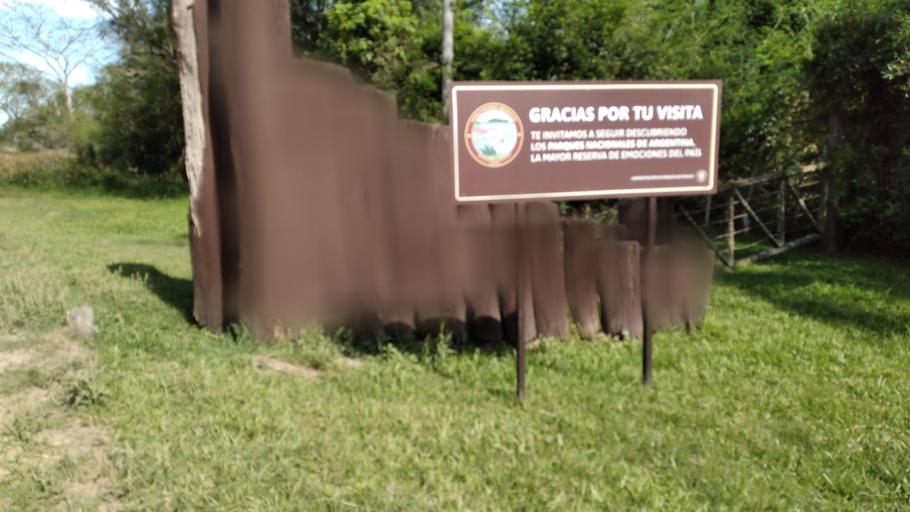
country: AR
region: Corrientes
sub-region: Departamento de Mburucuya
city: Mburucuya
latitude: -28.0471
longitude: -58.1340
